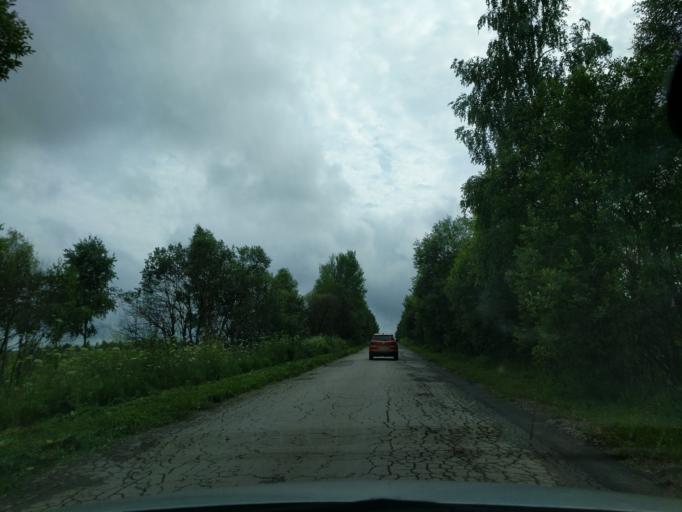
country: RU
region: Kaluga
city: Nikola-Lenivets
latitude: 54.7565
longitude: 35.6992
